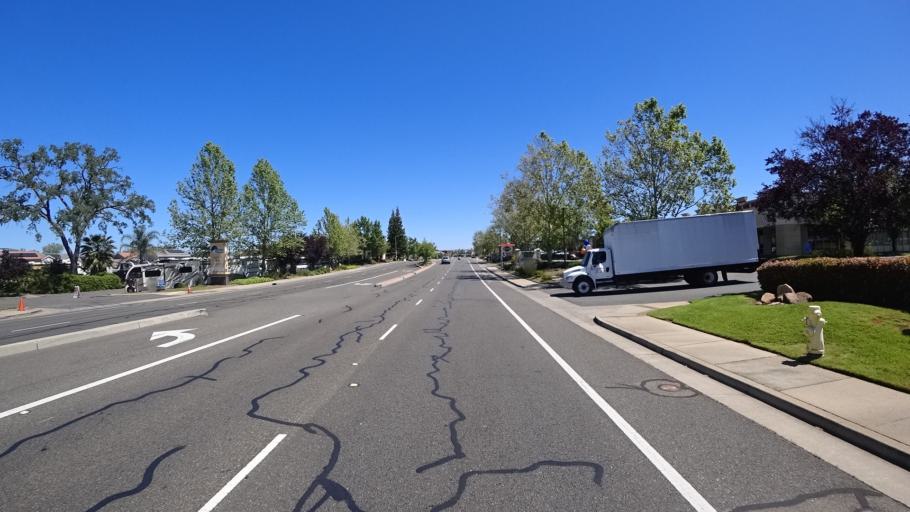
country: US
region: California
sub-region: Placer County
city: Rocklin
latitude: 38.7981
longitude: -121.2142
